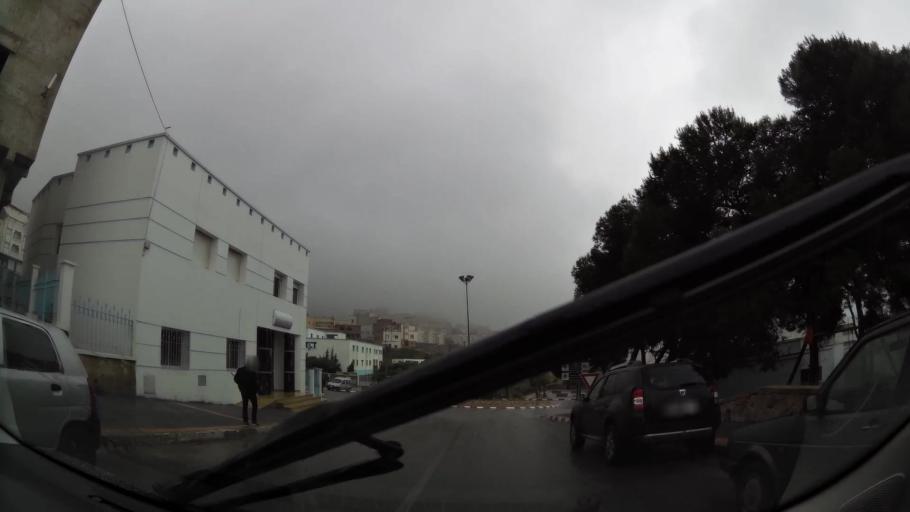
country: MA
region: Taza-Al Hoceima-Taounate
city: Al Hoceima
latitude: 35.2479
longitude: -3.9457
